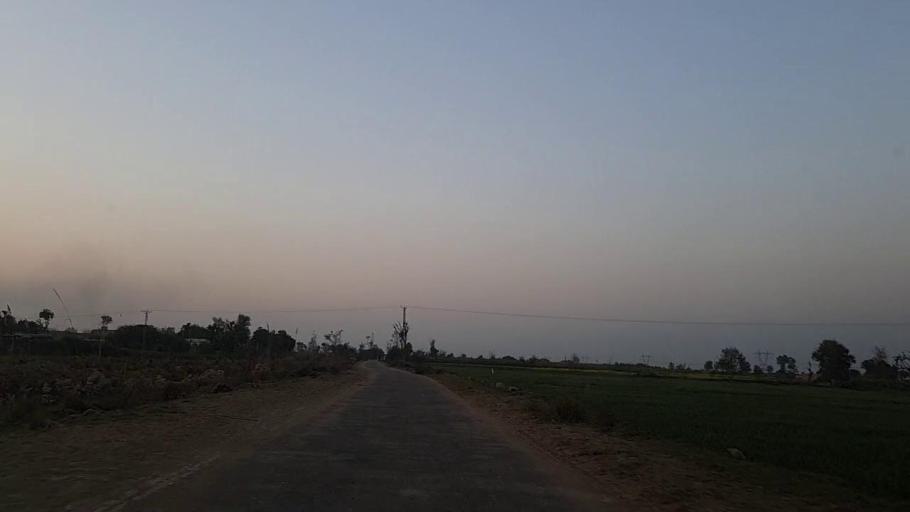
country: PK
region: Sindh
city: Hala
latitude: 25.9542
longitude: 68.4245
